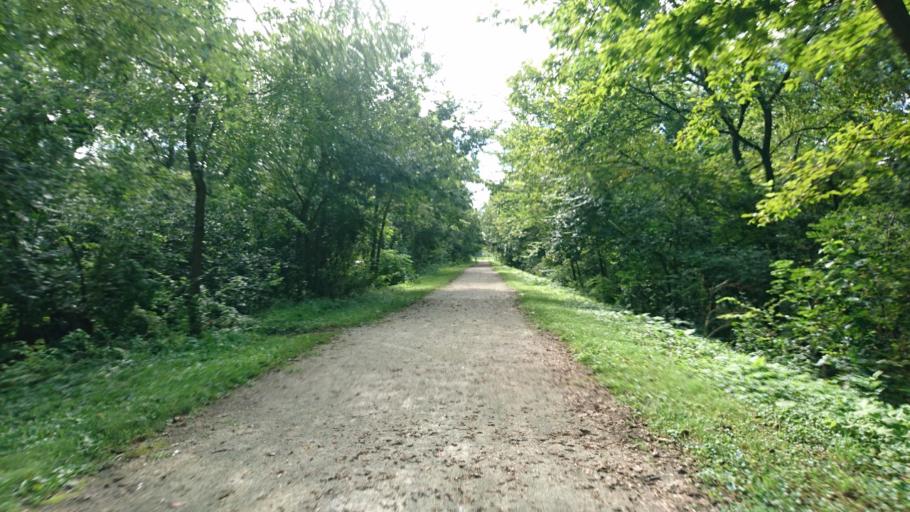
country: US
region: Illinois
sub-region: Will County
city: Manhattan
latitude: 41.4224
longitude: -87.9919
